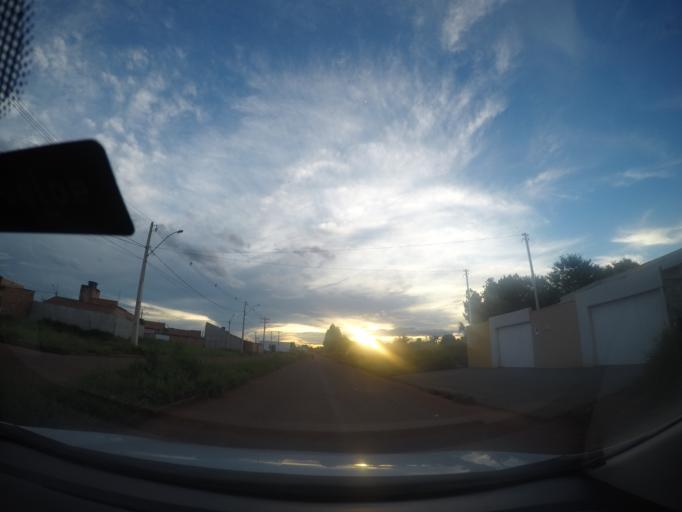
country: BR
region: Goias
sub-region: Goianira
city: Goianira
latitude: -16.5692
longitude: -49.3759
